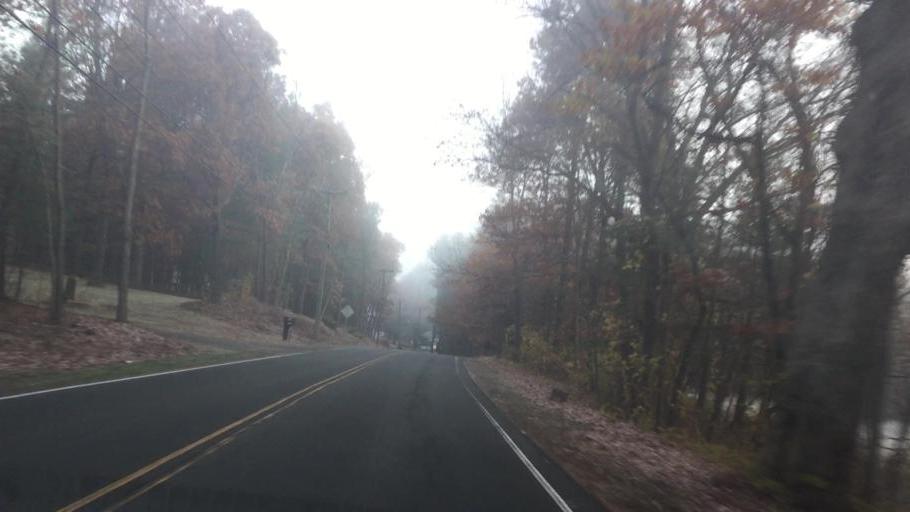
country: US
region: Massachusetts
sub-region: Hampshire County
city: Southampton
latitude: 42.2212
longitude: -72.6887
